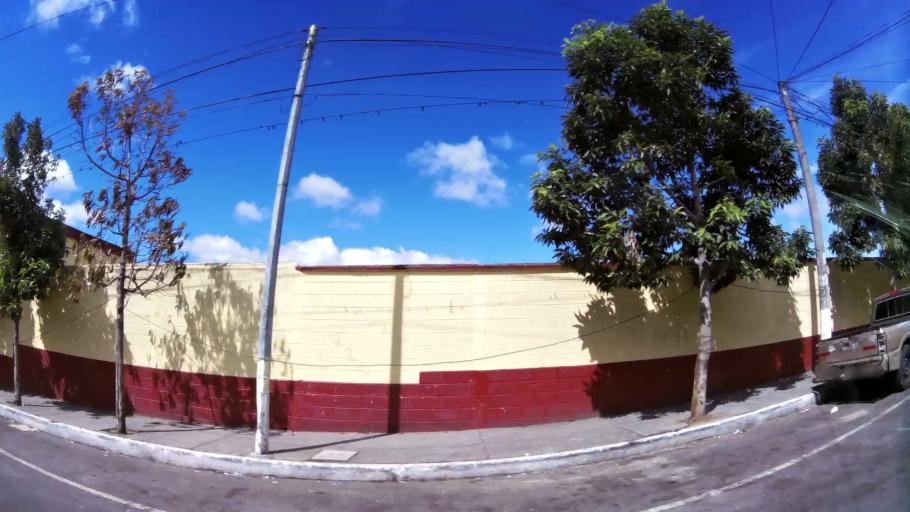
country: GT
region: Guatemala
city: Guatemala City
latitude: 14.6016
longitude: -90.5424
